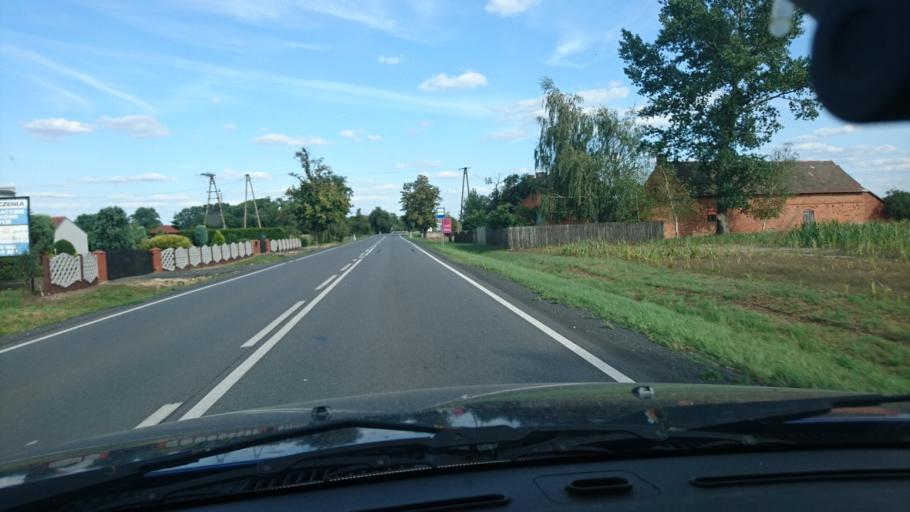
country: PL
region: Greater Poland Voivodeship
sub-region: Powiat krotoszynski
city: Zduny
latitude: 51.7192
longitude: 17.3619
